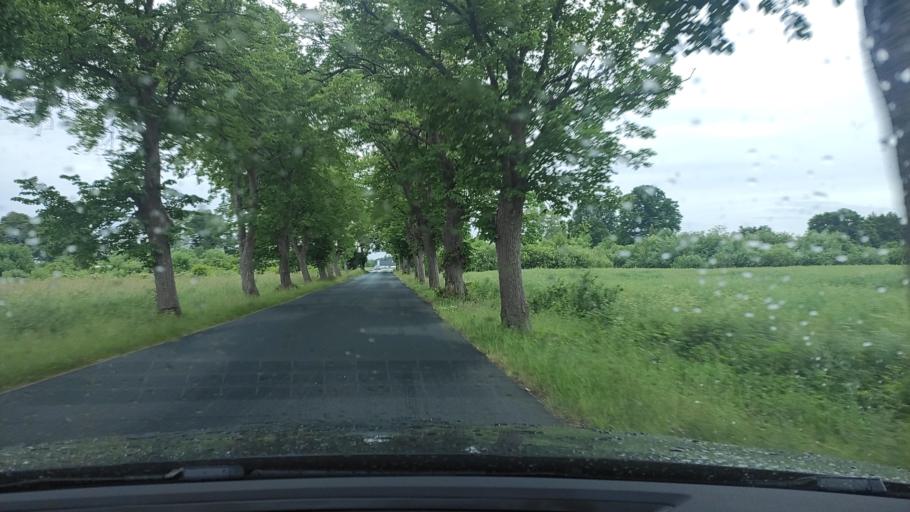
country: PL
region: West Pomeranian Voivodeship
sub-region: Powiat slawienski
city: Slawno
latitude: 54.5114
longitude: 16.5790
